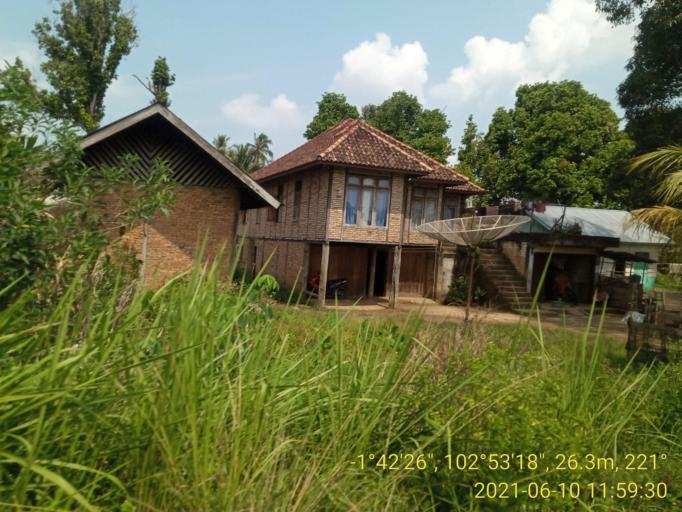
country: ID
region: Jambi
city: Mersam
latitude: -1.7072
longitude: 102.8885
